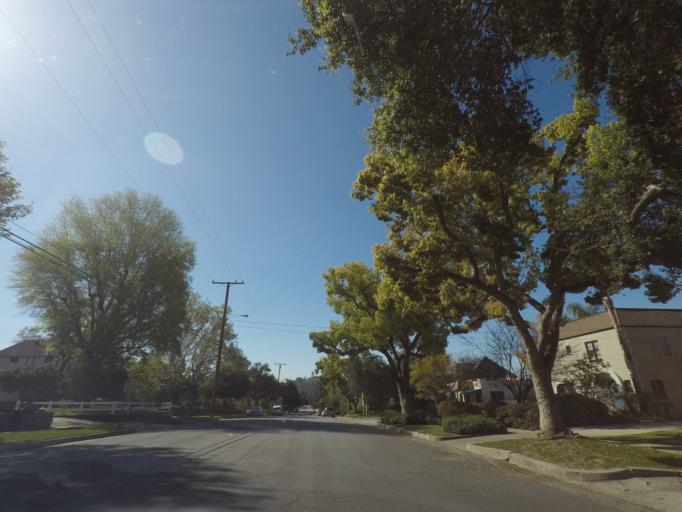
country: US
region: California
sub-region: Los Angeles County
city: South Pasadena
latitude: 34.1215
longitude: -118.1633
